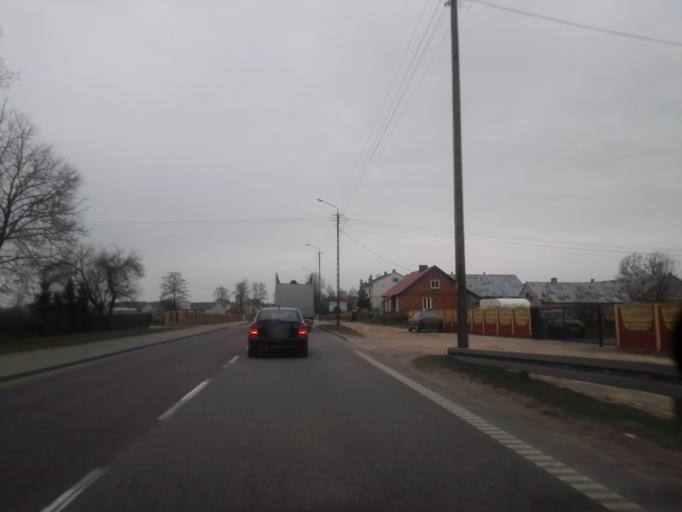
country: PL
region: Podlasie
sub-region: Powiat grajewski
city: Grajewo
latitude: 53.6246
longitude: 22.4051
